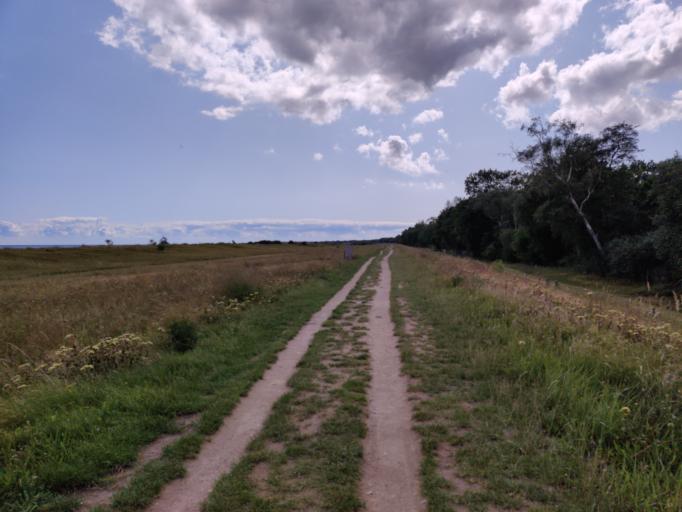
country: DK
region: Zealand
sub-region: Guldborgsund Kommune
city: Nykobing Falster
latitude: 54.6880
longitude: 11.9682
